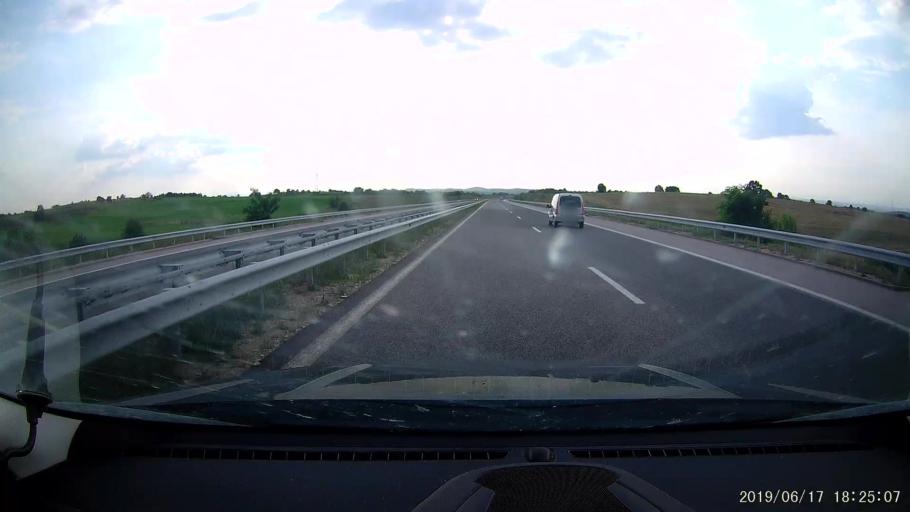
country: BG
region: Khaskovo
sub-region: Obshtina Dimitrovgrad
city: Dimitrovgrad
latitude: 41.9894
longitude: 25.6706
